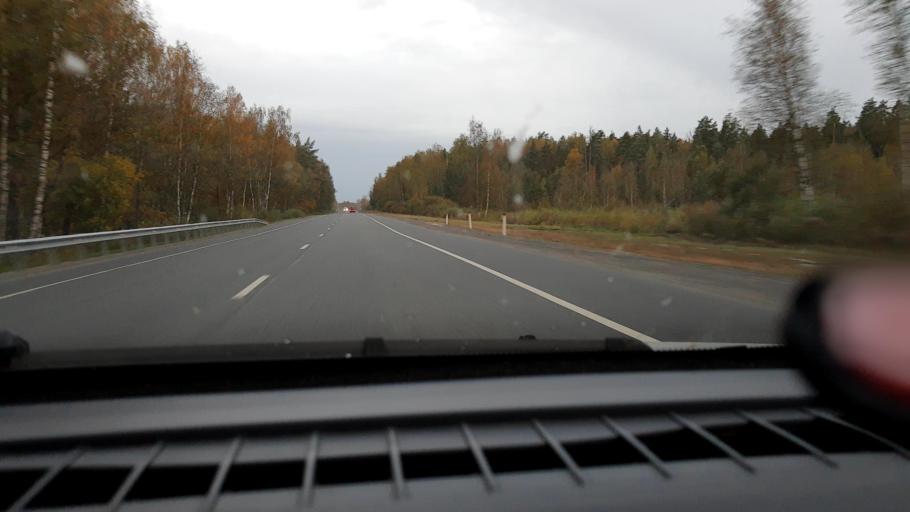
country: RU
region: Vladimir
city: Orgtrud
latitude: 56.2069
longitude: 40.6953
